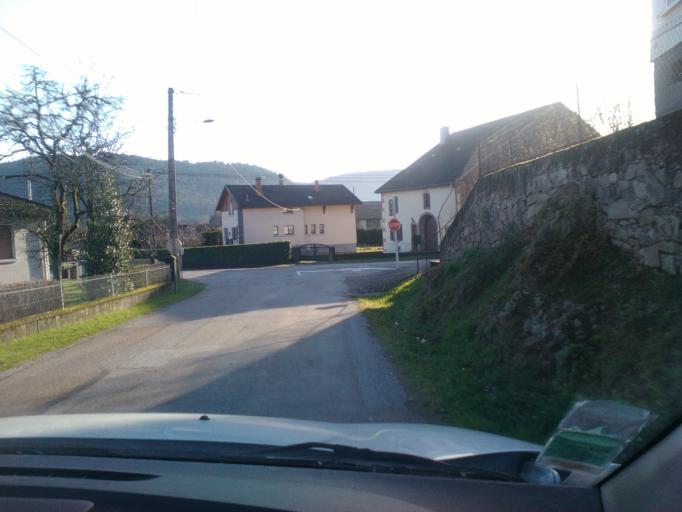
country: FR
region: Lorraine
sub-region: Departement des Vosges
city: Saint-Ame
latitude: 48.0238
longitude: 6.6577
